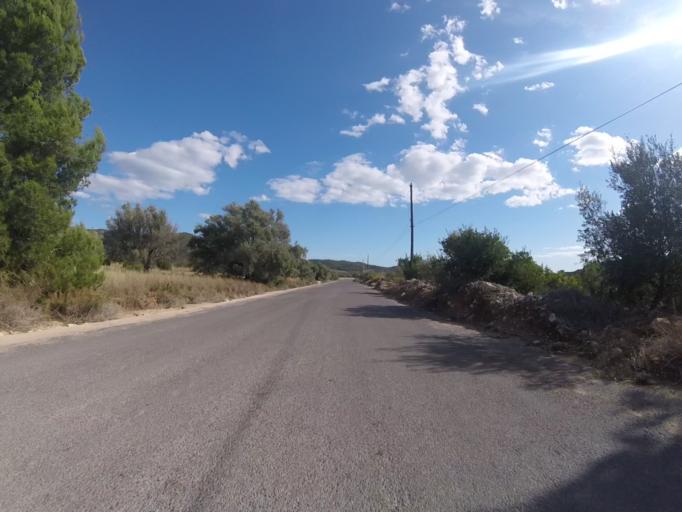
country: ES
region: Valencia
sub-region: Provincia de Castello
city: Alcala de Xivert
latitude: 40.2707
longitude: 0.2391
